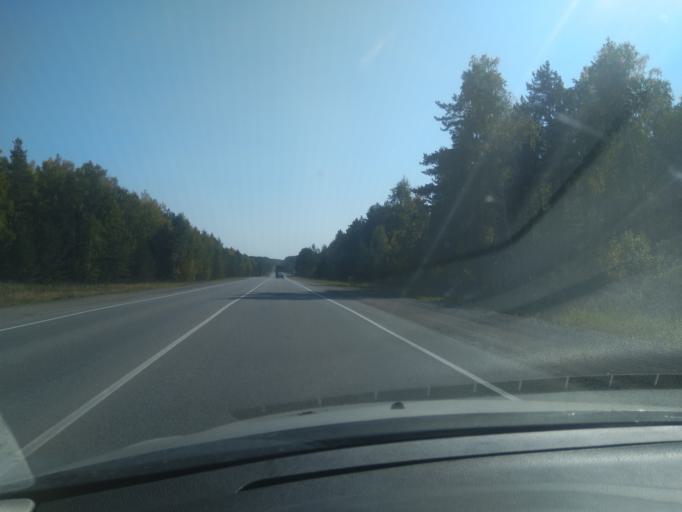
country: RU
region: Sverdlovsk
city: Verkhneye Dubrovo
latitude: 56.7021
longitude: 61.0806
